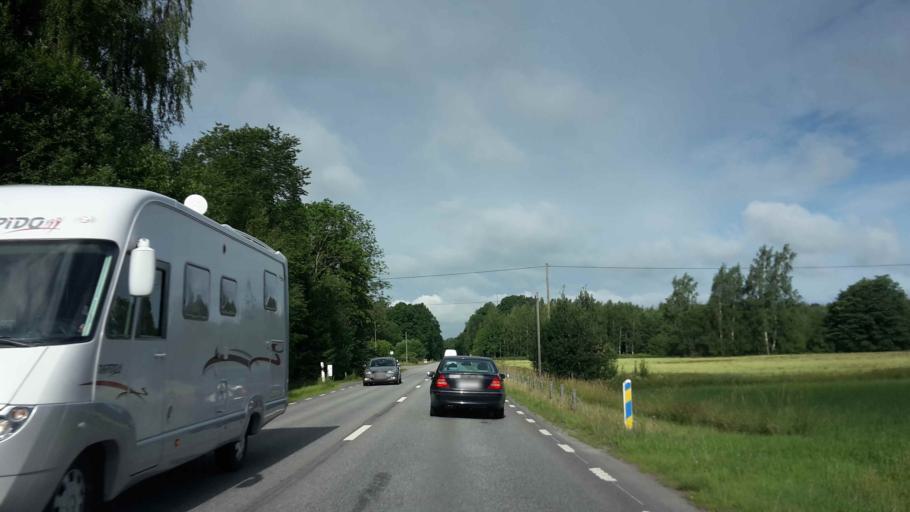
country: SE
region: OEstergoetland
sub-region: Motala Kommun
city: Borensberg
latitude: 58.5817
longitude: 15.1781
